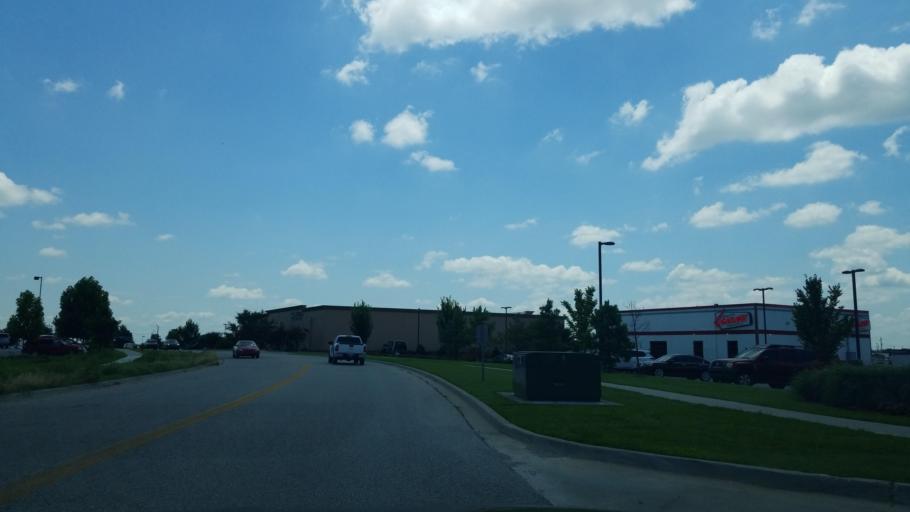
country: US
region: Oklahoma
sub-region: Tulsa County
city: Broken Arrow
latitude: 36.0677
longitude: -95.7828
